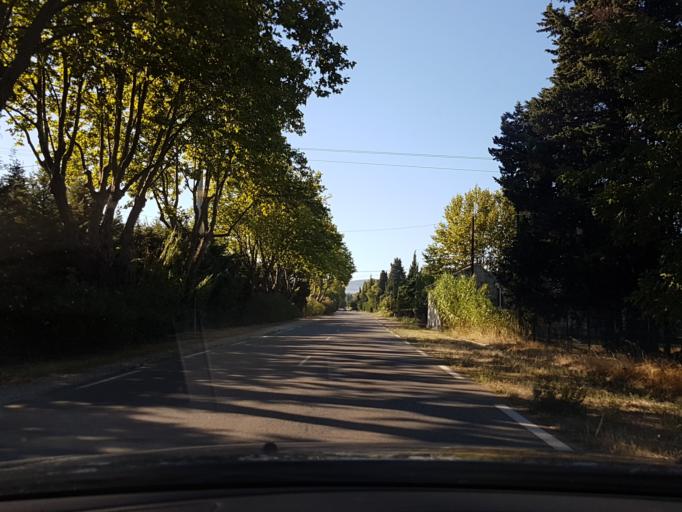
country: FR
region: Provence-Alpes-Cote d'Azur
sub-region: Departement des Bouches-du-Rhone
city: Molleges
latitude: 43.7864
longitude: 4.9544
